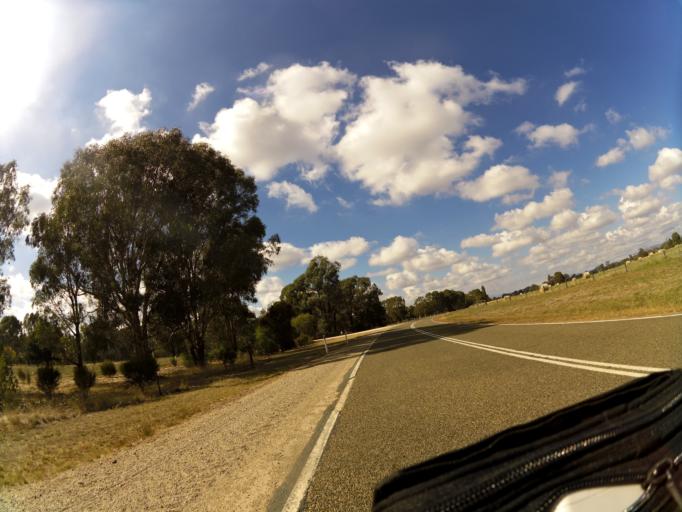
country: AU
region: Victoria
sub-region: Benalla
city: Benalla
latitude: -36.5826
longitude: 146.0079
